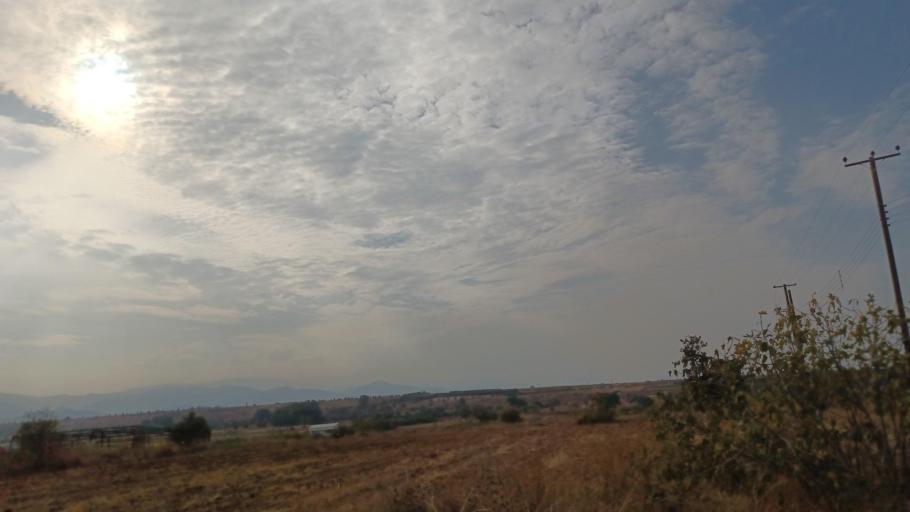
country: CY
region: Lefkosia
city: Peristerona
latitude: 35.1168
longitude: 33.0934
